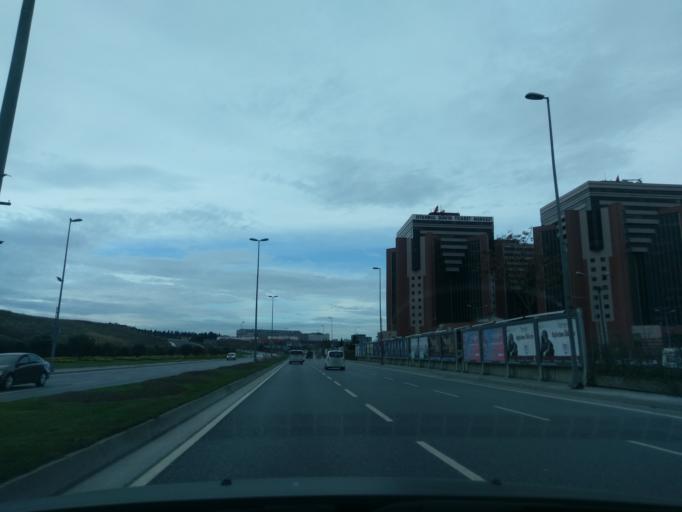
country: TR
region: Istanbul
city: Bahcelievler
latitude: 40.9840
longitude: 28.8333
